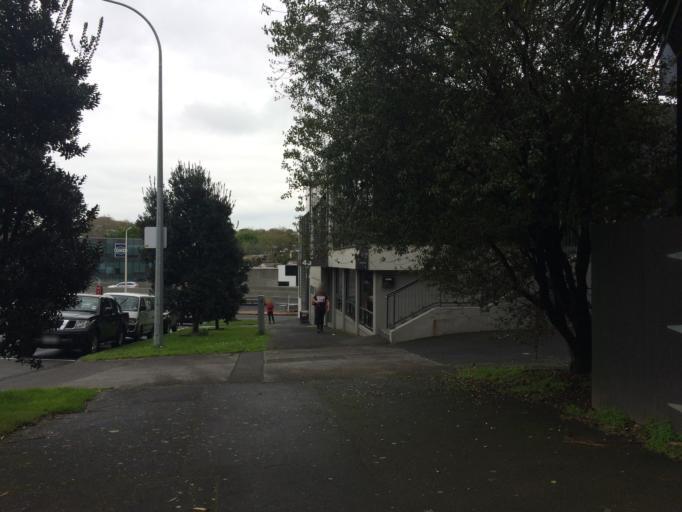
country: NZ
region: Auckland
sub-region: Auckland
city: Auckland
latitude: -36.8496
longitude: 174.7546
